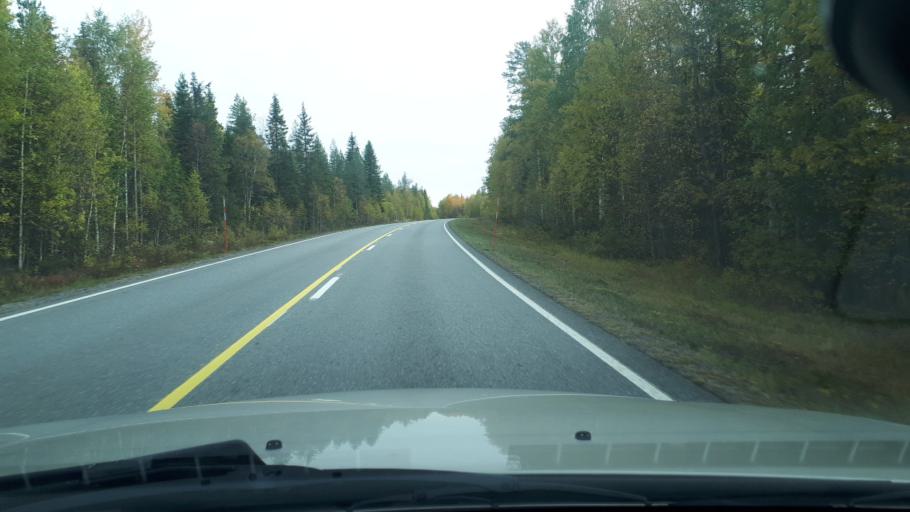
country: FI
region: Lapland
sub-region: Rovaniemi
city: Ranua
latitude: 66.0095
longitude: 26.2853
